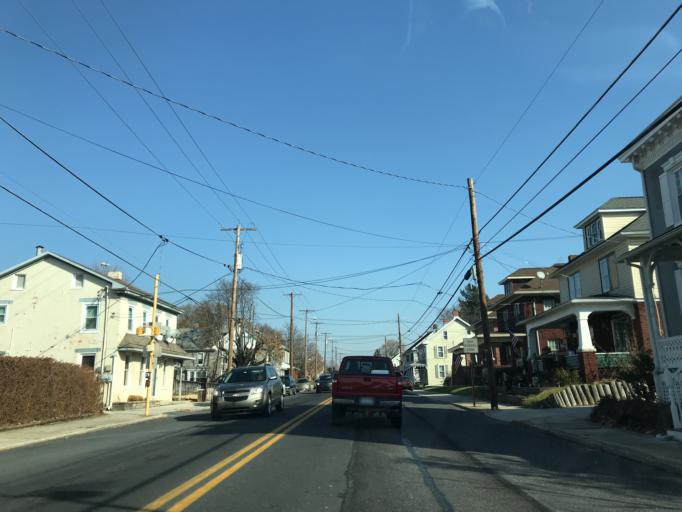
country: US
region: Pennsylvania
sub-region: Adams County
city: Littlestown
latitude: 39.7472
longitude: -77.0825
